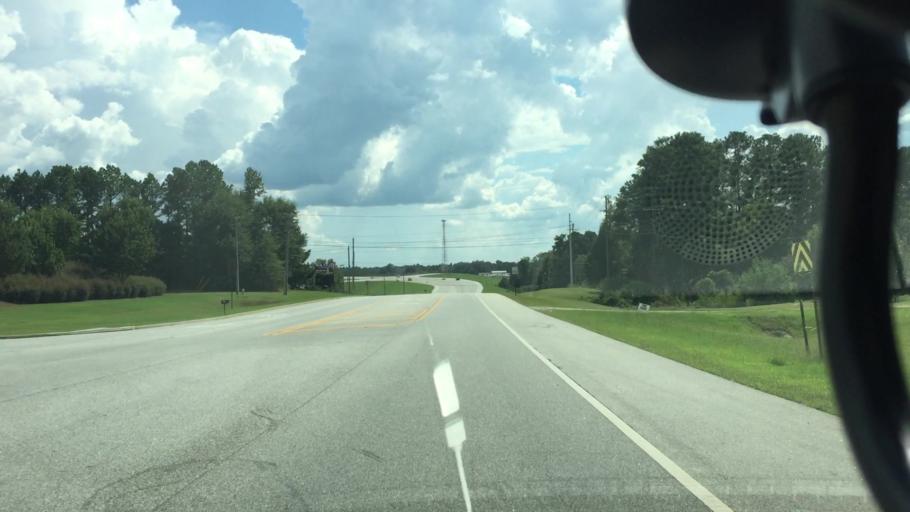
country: US
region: Alabama
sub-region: Lee County
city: Auburn
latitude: 32.5556
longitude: -85.5281
